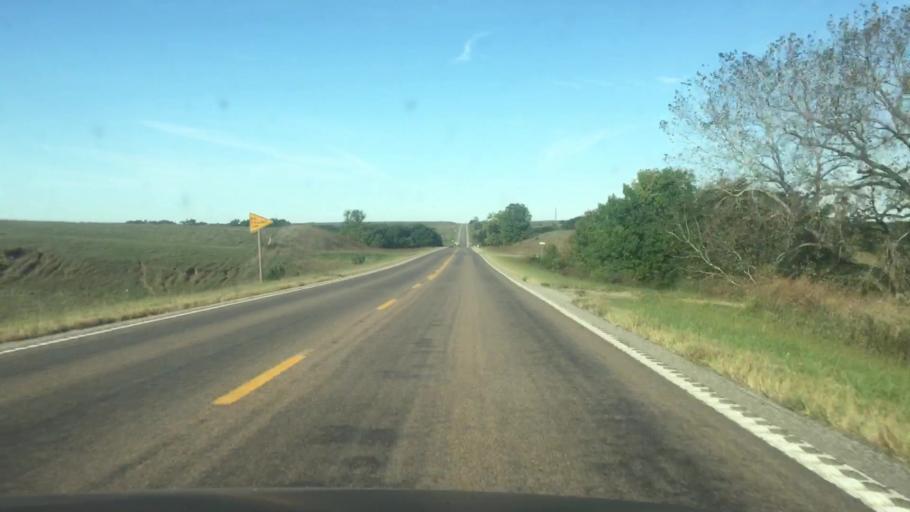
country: US
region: Nebraska
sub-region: Thayer County
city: Hebron
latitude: 40.1472
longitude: -97.5138
